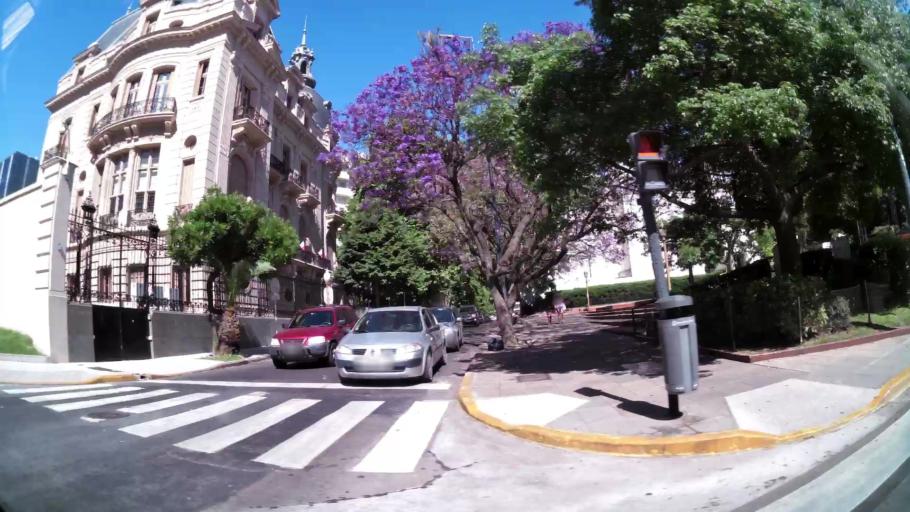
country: AR
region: Buenos Aires F.D.
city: Retiro
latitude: -34.5916
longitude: -58.3822
